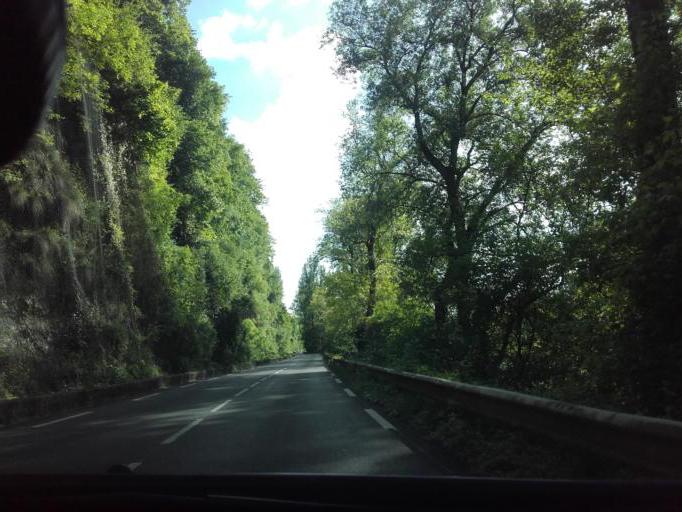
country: FR
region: Aquitaine
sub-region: Departement de la Dordogne
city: Lalinde
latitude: 44.8506
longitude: 0.8034
